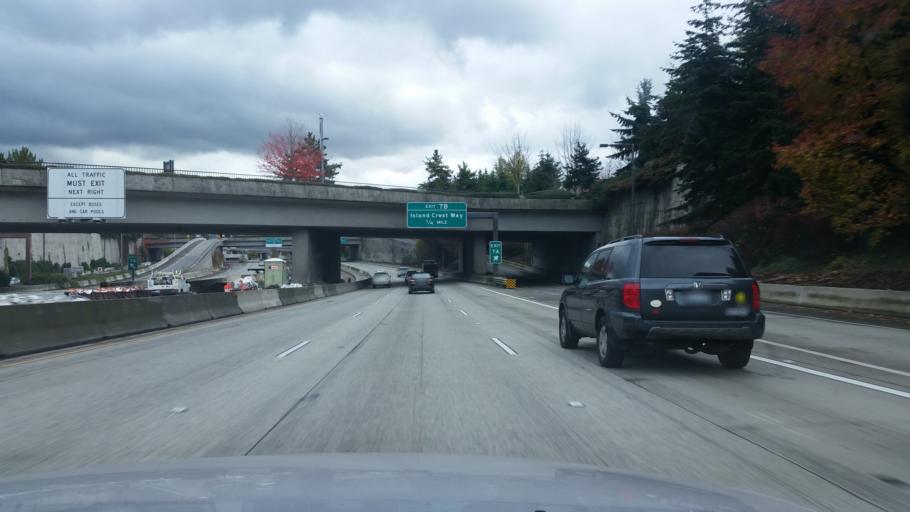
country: US
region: Washington
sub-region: King County
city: Mercer Island
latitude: 47.5902
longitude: -122.2388
